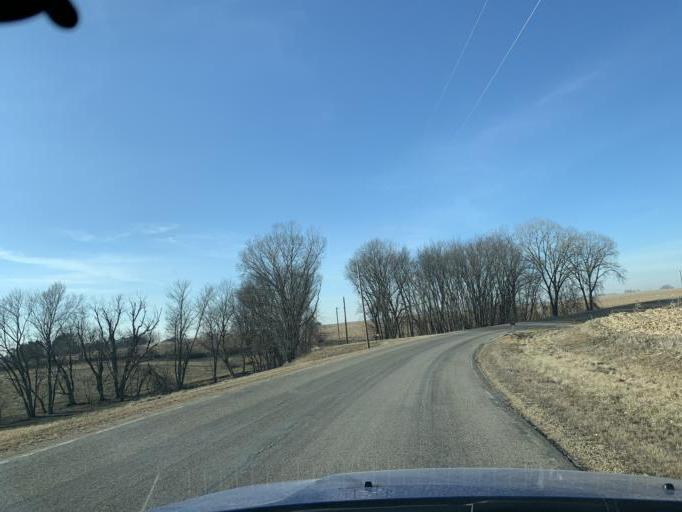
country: US
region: Wisconsin
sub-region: Iowa County
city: Barneveld
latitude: 42.8207
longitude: -89.9294
